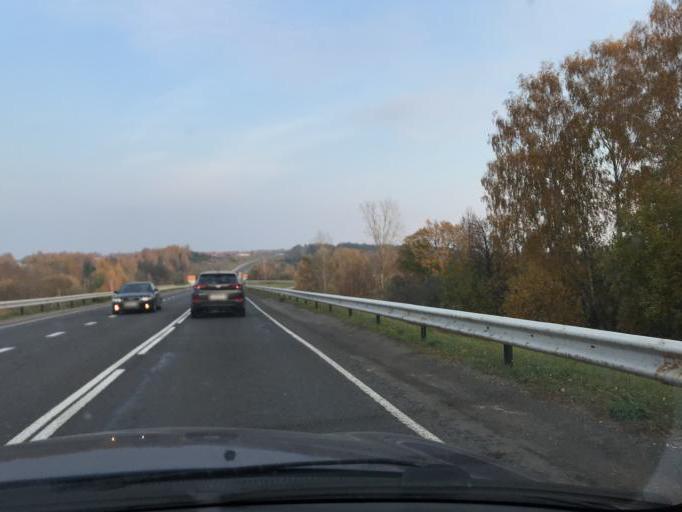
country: BY
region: Grodnenskaya
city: Karelichy
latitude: 53.5960
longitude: 26.0446
